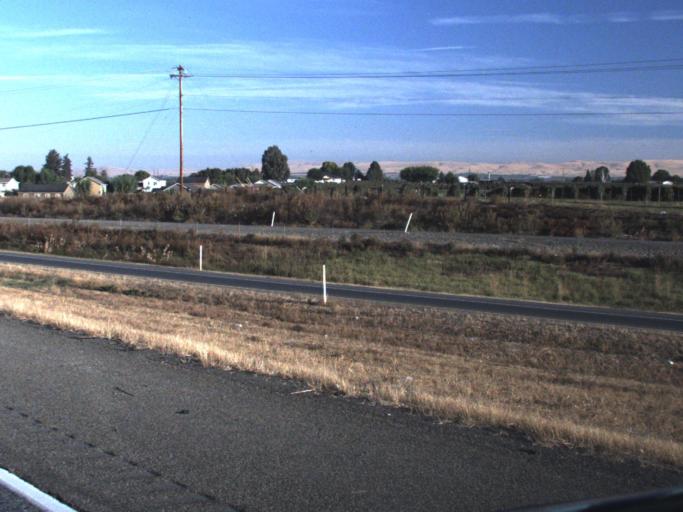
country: US
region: Washington
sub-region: Yakima County
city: Granger
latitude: 46.3474
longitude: -120.1798
